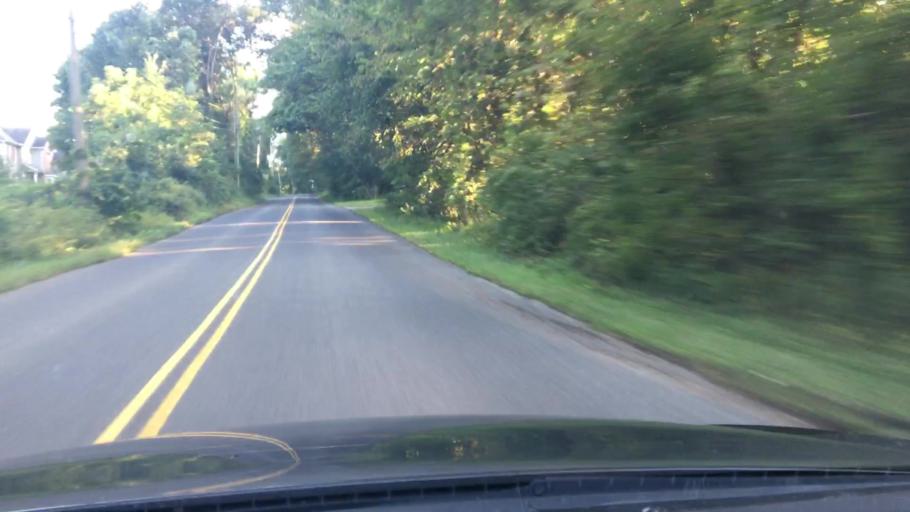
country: US
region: Connecticut
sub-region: Litchfield County
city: New Milford
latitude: 41.6169
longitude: -73.3734
